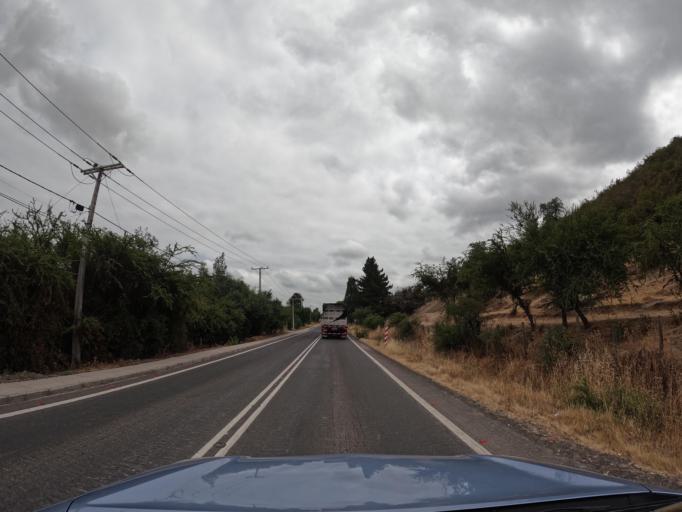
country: CL
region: Maule
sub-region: Provincia de Curico
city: Teno
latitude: -34.8000
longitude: -71.2243
